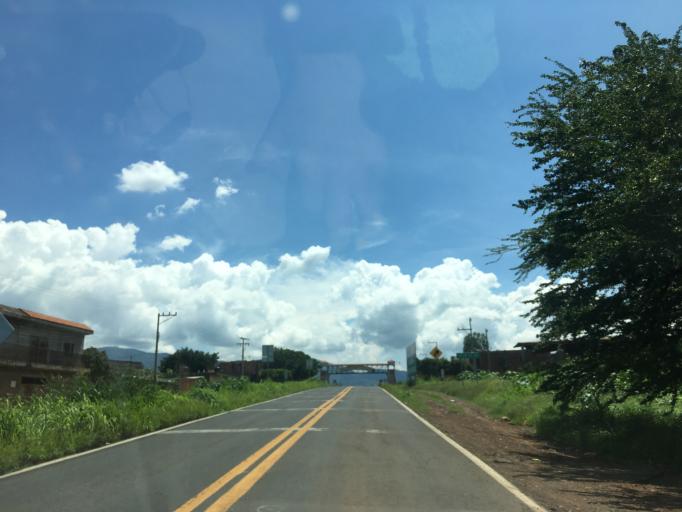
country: MX
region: Nayarit
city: Ixtlan del Rio
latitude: 21.0313
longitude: -104.3519
